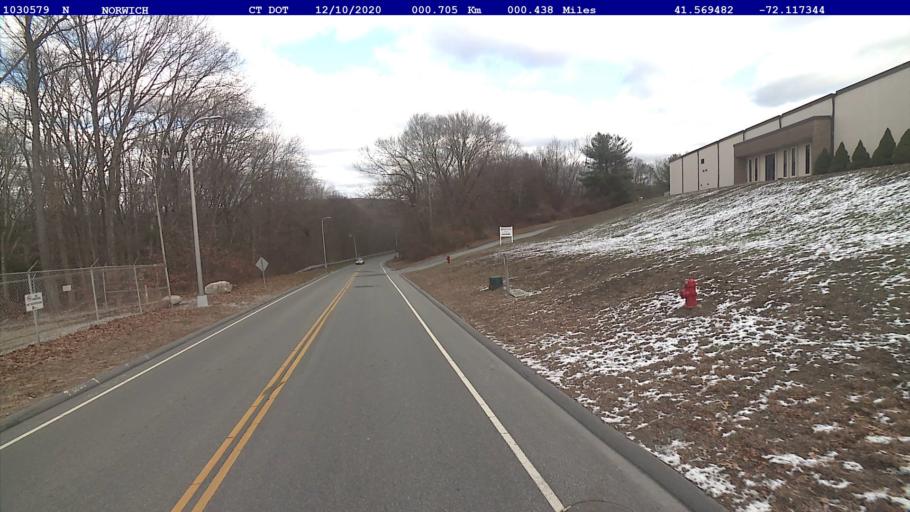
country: US
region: Connecticut
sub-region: New London County
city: Baltic
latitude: 41.5695
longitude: -72.1173
